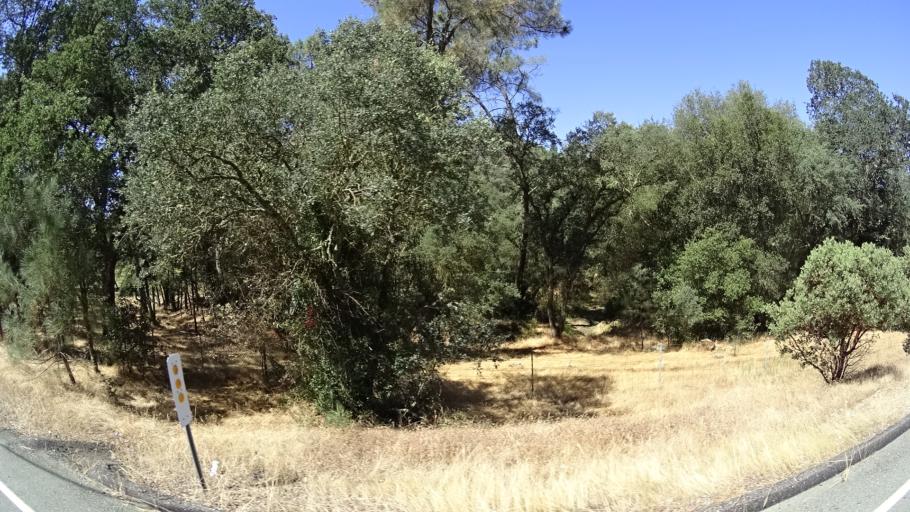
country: US
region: California
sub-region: Calaveras County
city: Valley Springs
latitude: 38.2153
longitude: -120.8809
